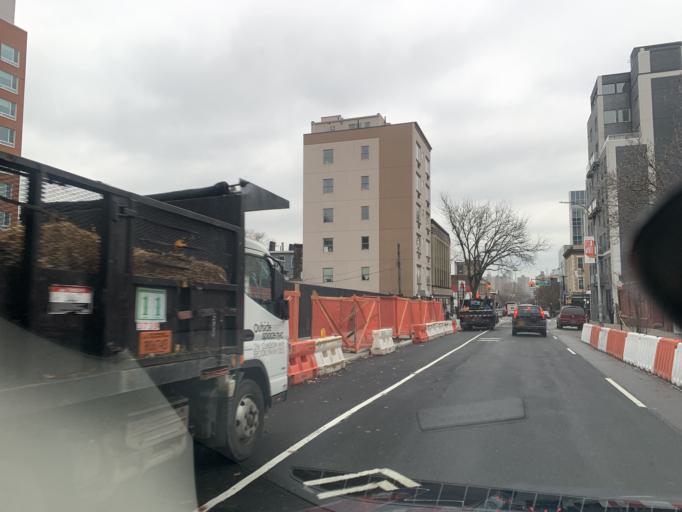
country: US
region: New York
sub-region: Kings County
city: Brooklyn
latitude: 40.6932
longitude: -73.9609
